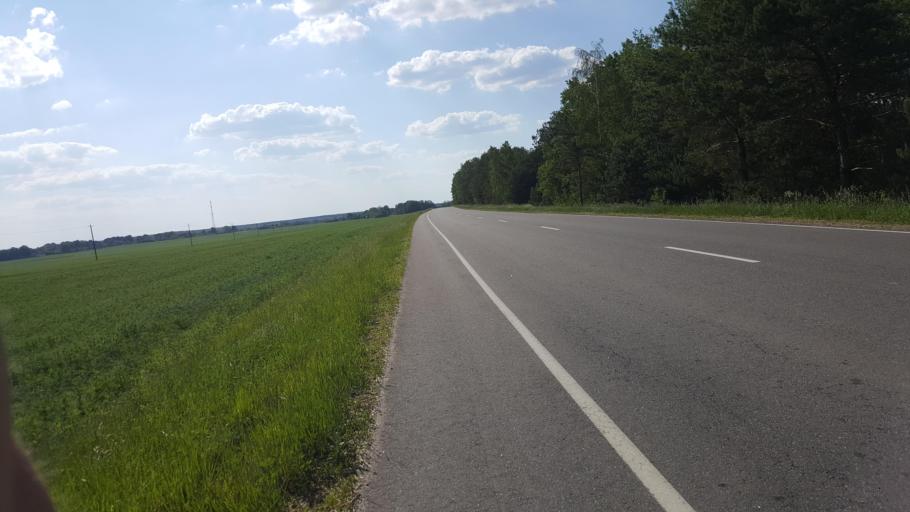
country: BY
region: Brest
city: Zhabinka
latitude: 52.3556
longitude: 24.1761
